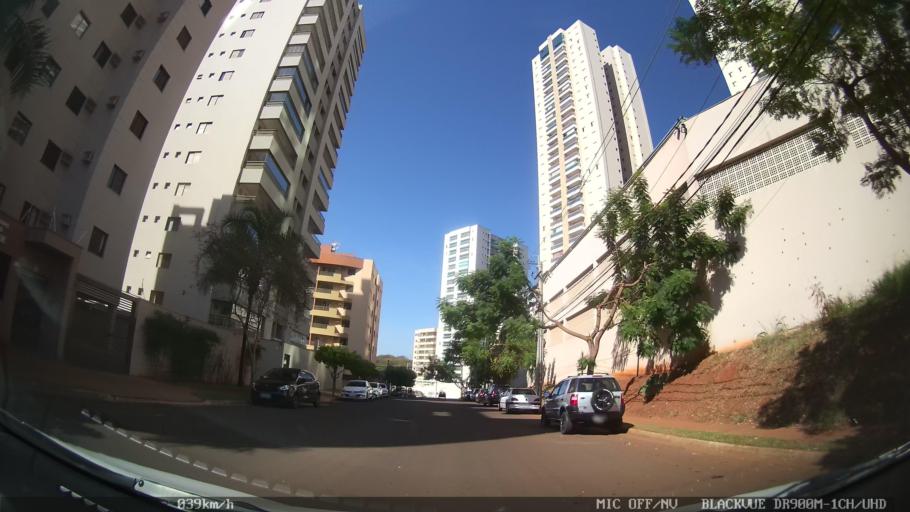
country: BR
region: Sao Paulo
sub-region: Ribeirao Preto
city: Ribeirao Preto
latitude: -21.2079
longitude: -47.7958
